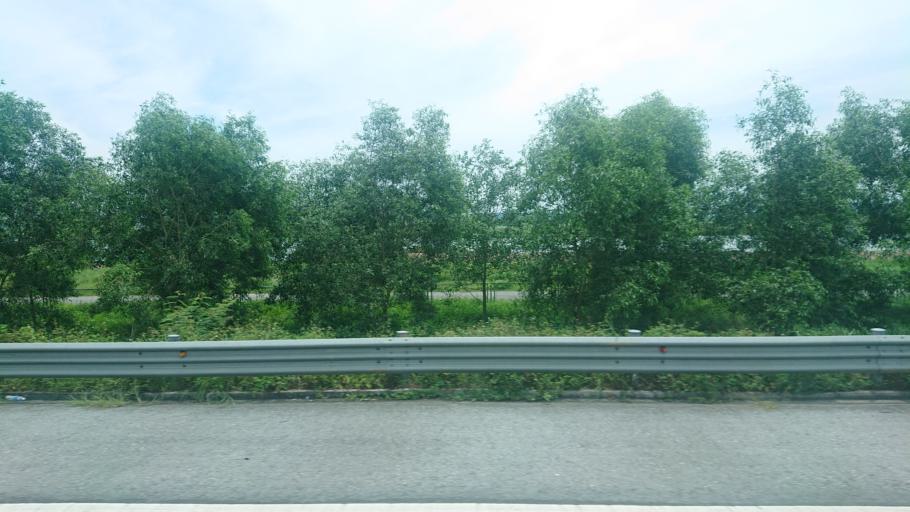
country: VN
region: Hai Phong
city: An Lao
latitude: 20.7806
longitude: 106.5695
